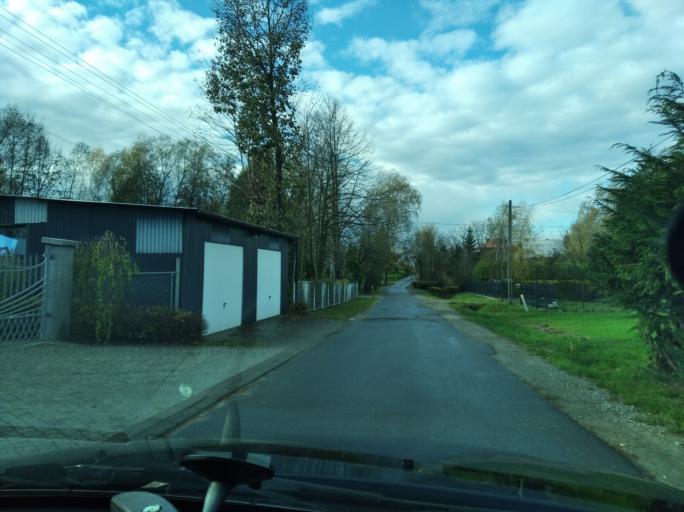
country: PL
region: Subcarpathian Voivodeship
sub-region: Powiat debicki
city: Debica
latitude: 50.0406
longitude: 21.4446
